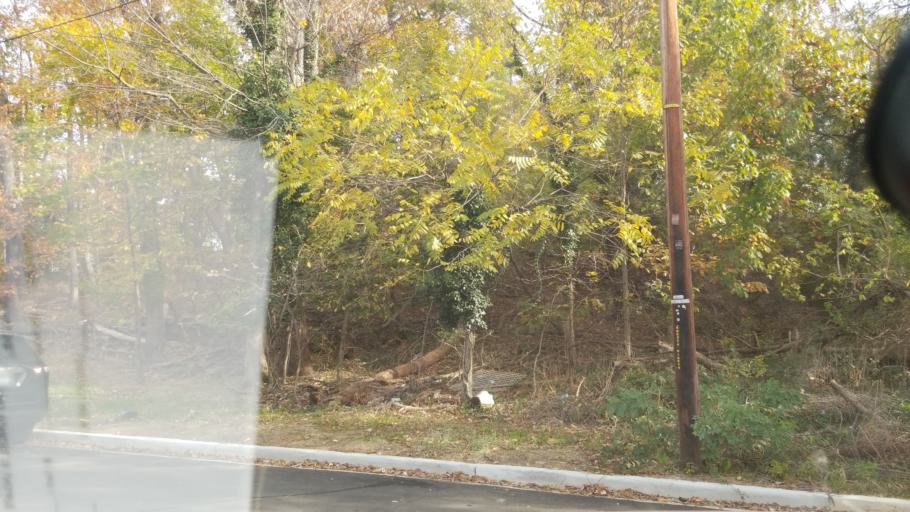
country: US
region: Maryland
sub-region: Prince George's County
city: Hillcrest Heights
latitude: 38.8630
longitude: -76.9790
